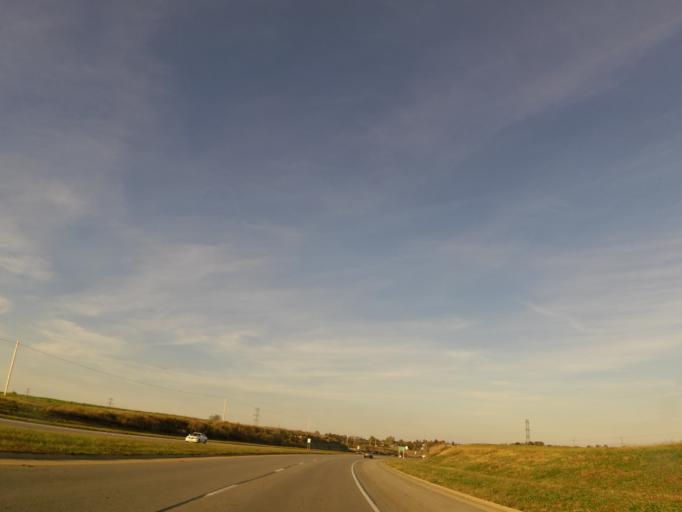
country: US
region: Kentucky
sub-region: Garrard County
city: Lancaster
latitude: 37.7006
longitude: -84.6650
